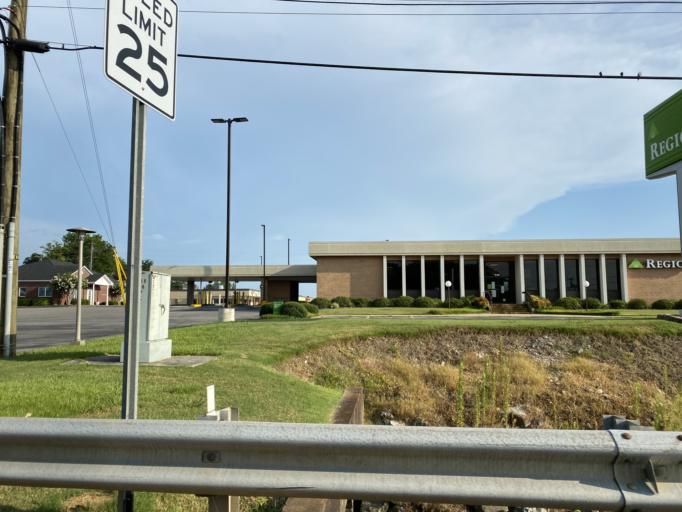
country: US
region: Alabama
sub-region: Morgan County
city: Hartselle
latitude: 34.4426
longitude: -86.9411
